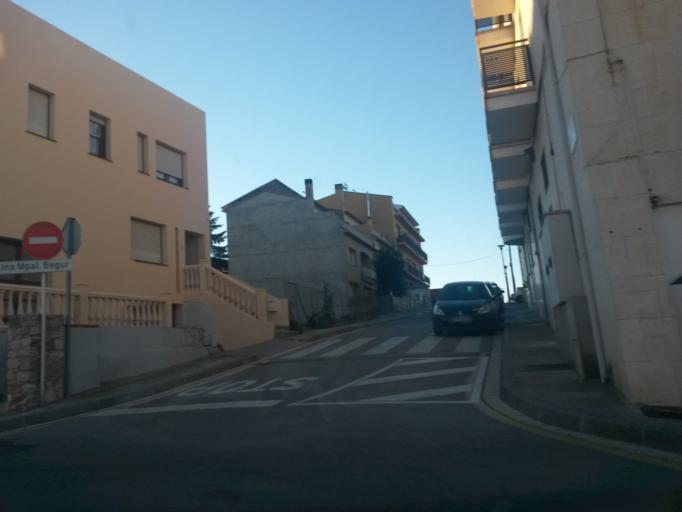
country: ES
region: Catalonia
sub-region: Provincia de Girona
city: Begur
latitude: 41.9523
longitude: 3.2064
